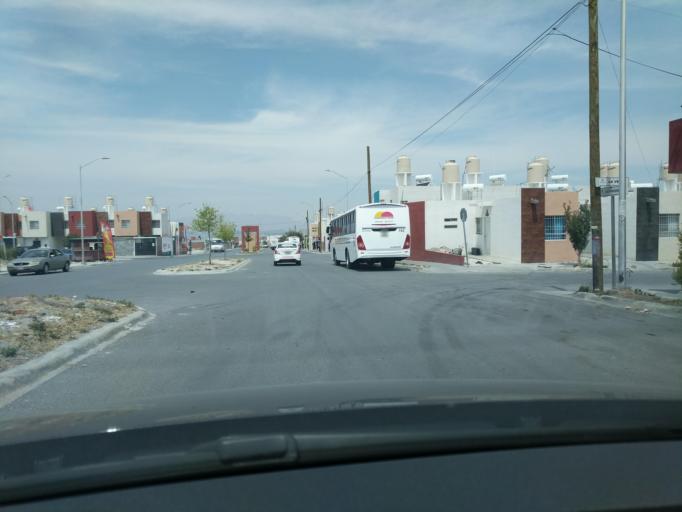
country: MX
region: Coahuila
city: Saltillo
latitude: 25.3469
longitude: -101.0088
